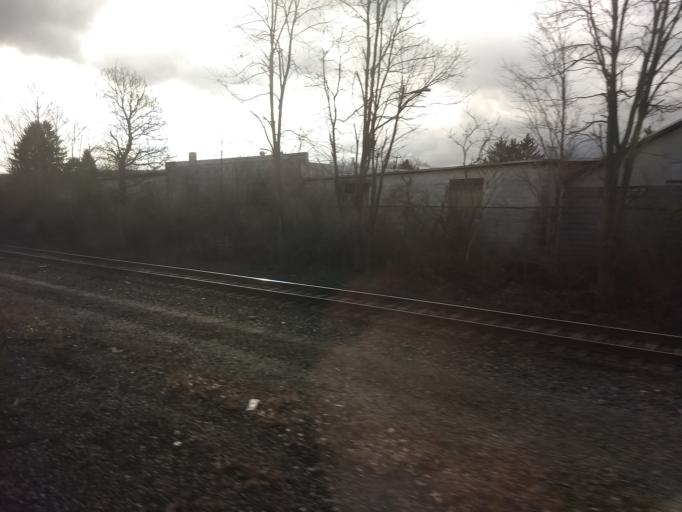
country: US
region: Pennsylvania
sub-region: Cambria County
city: Portage
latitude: 40.3898
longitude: -78.6756
